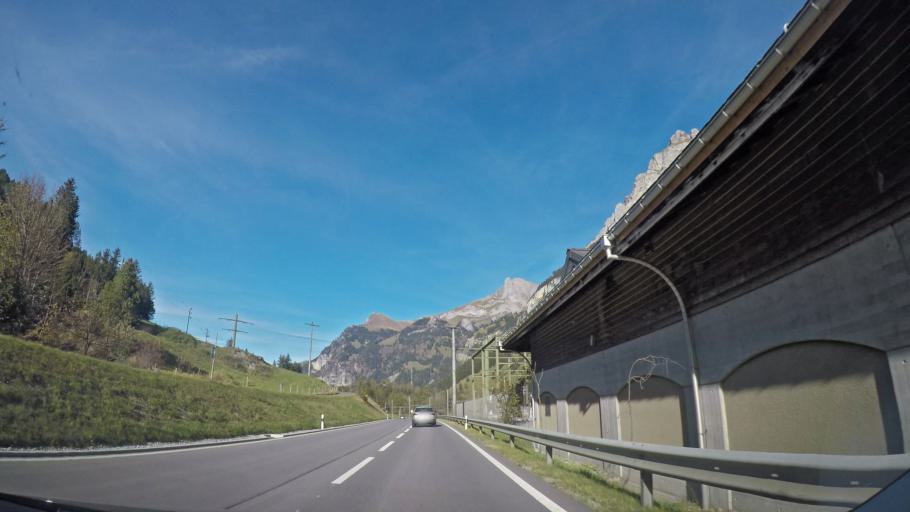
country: CH
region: Bern
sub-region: Frutigen-Niedersimmental District
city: Kandersteg
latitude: 46.5029
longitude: 7.6742
